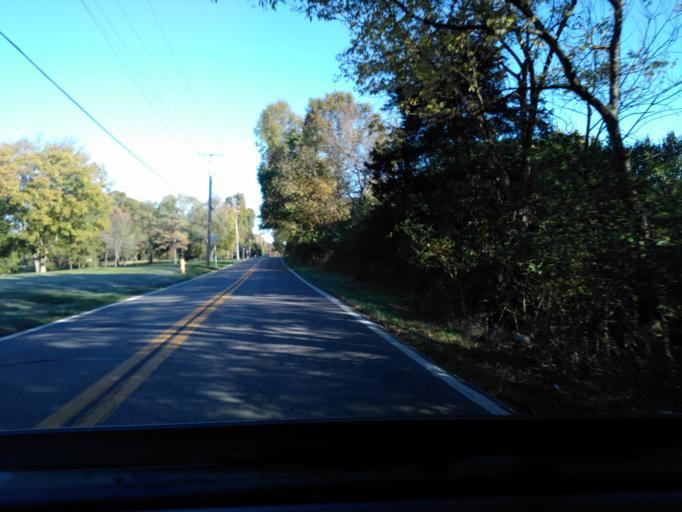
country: US
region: Missouri
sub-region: Saint Louis County
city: Town and Country
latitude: 38.6062
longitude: -90.4854
